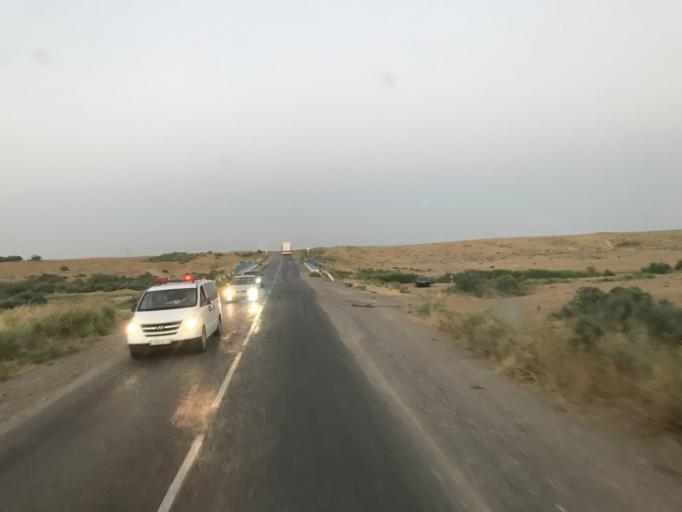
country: UZ
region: Toshkent
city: Chinoz
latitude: 41.1991
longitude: 68.6094
